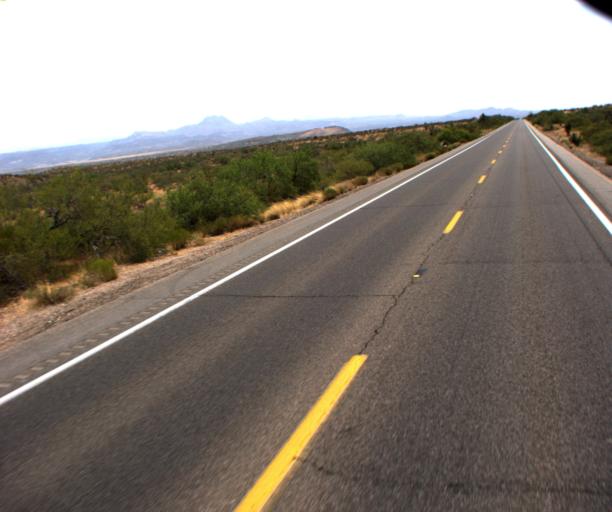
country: US
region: Arizona
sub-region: Gila County
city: Peridot
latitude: 33.3234
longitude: -110.5460
